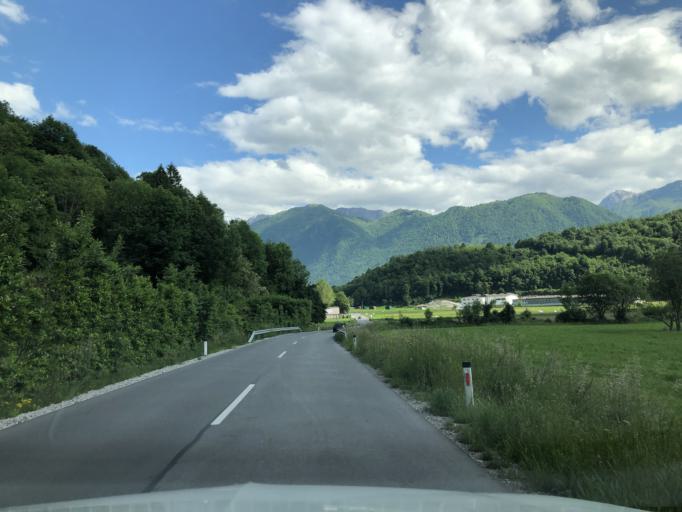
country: SI
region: Tolmin
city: Tolmin
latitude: 46.1655
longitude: 13.7098
